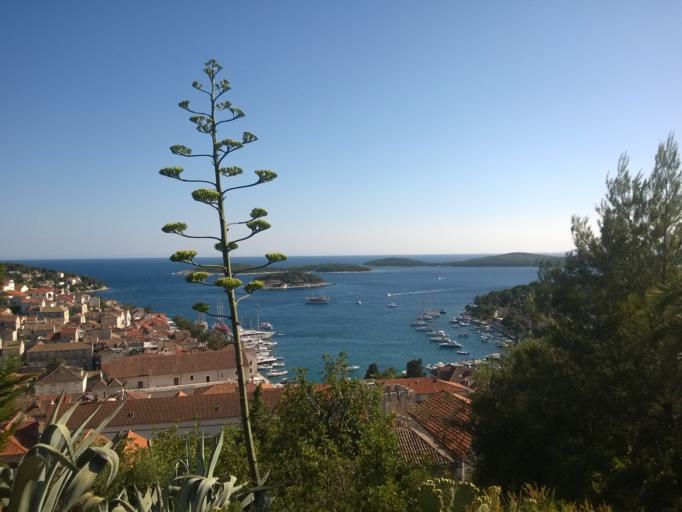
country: HR
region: Splitsko-Dalmatinska
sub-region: Grad Hvar
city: Hvar
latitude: 43.1740
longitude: 16.4422
